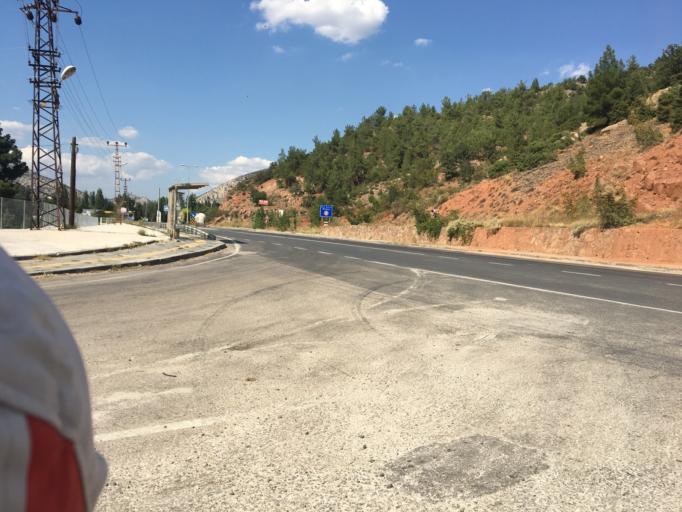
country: TR
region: Ankara
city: Nallihan
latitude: 40.1776
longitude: 31.3443
